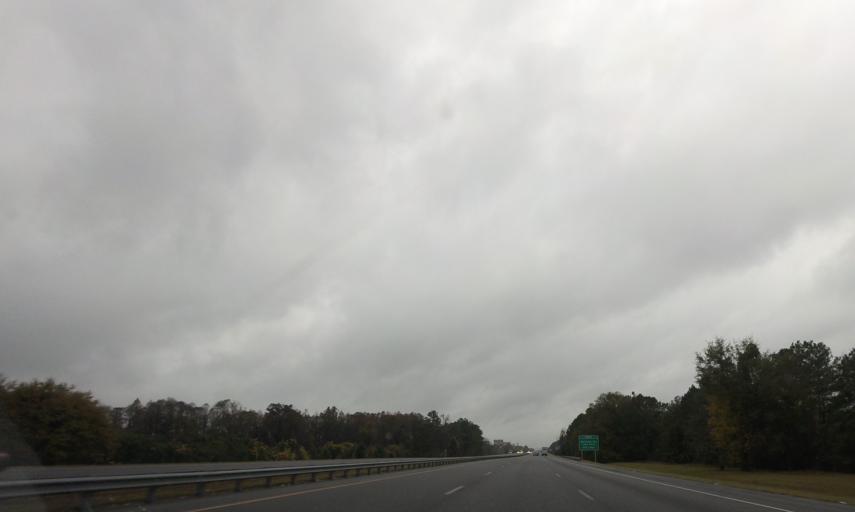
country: US
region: Georgia
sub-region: Echols County
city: Statenville
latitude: 30.6296
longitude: -83.1761
